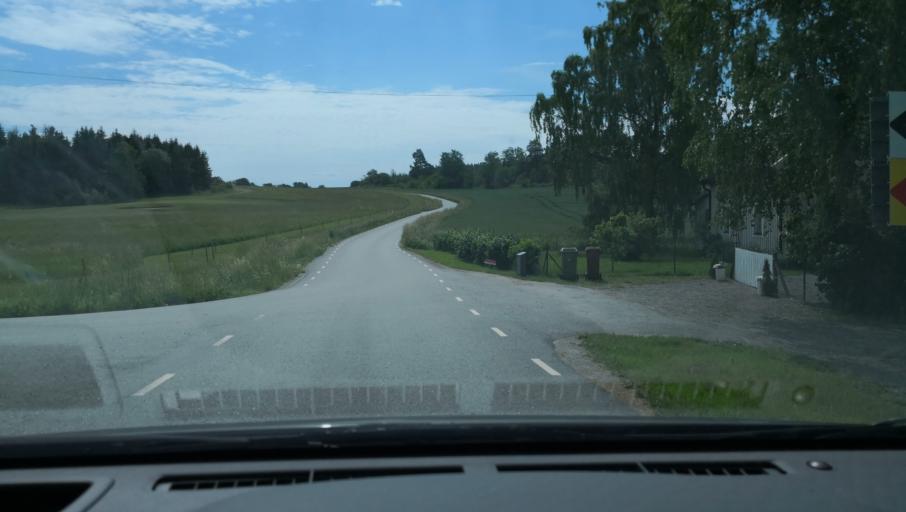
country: SE
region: Uppsala
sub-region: Habo Kommun
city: Balsta
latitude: 59.7047
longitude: 17.4758
